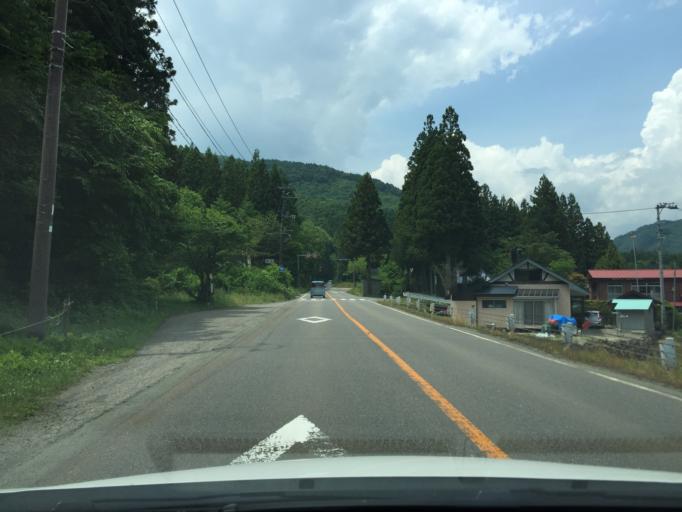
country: JP
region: Fukushima
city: Inawashiro
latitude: 37.6097
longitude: 140.1202
